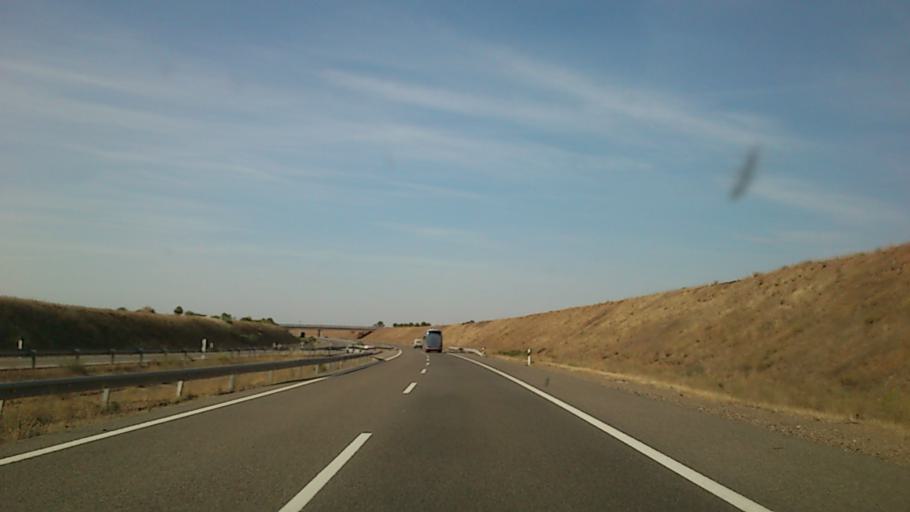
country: ES
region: Aragon
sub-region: Provincia de Zaragoza
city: Carinena
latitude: 41.3297
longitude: -1.2030
